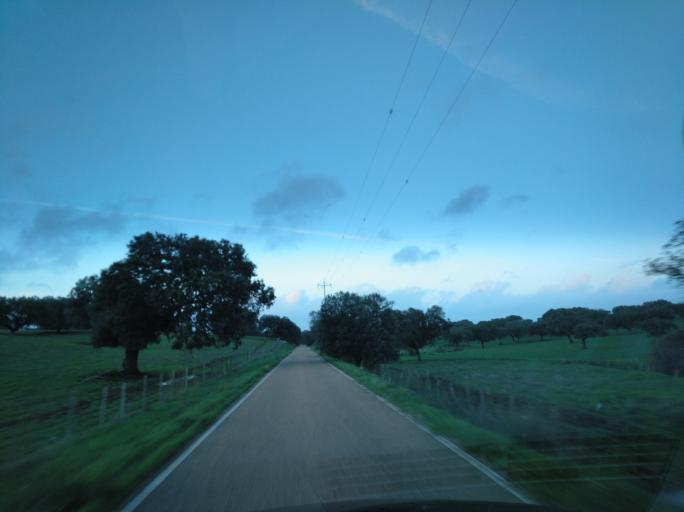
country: PT
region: Portalegre
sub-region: Campo Maior
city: Campo Maior
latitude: 39.0788
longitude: -7.1165
